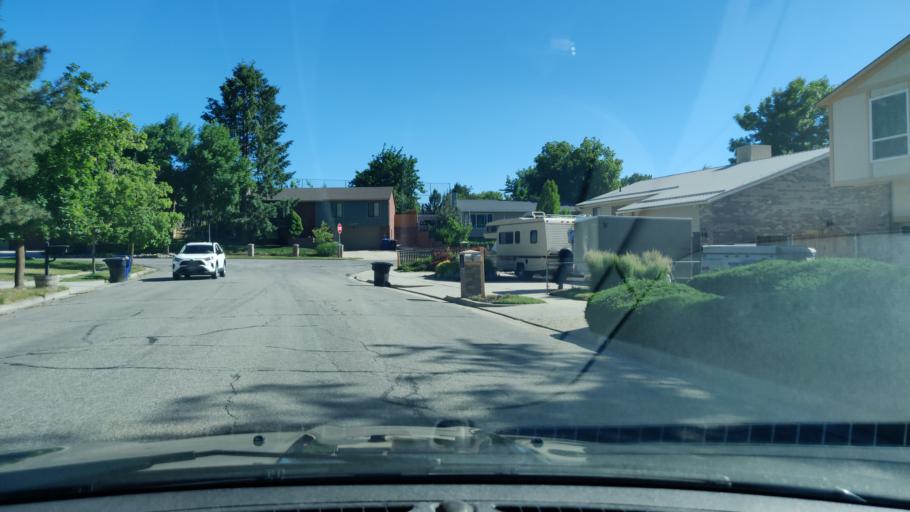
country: US
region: Utah
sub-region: Salt Lake County
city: Cottonwood Heights
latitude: 40.6212
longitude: -111.8046
